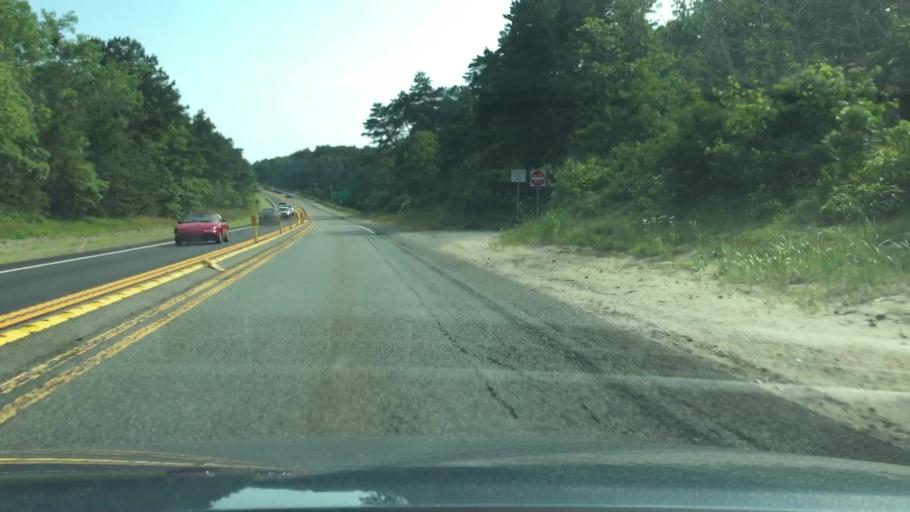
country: US
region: Massachusetts
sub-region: Barnstable County
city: East Harwich
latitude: 41.7357
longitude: -70.0232
